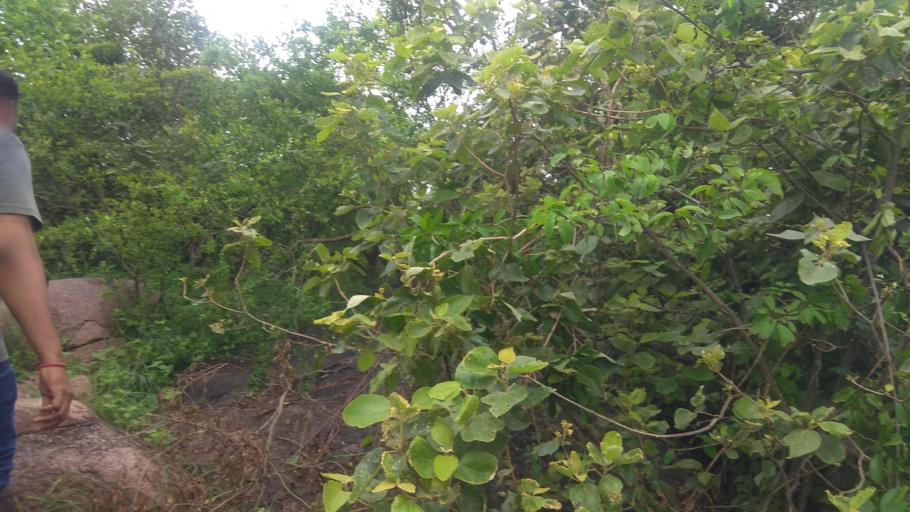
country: IN
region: Telangana
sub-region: Mahbubnagar
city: Farrukhnagar
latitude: 16.8974
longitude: 78.4972
